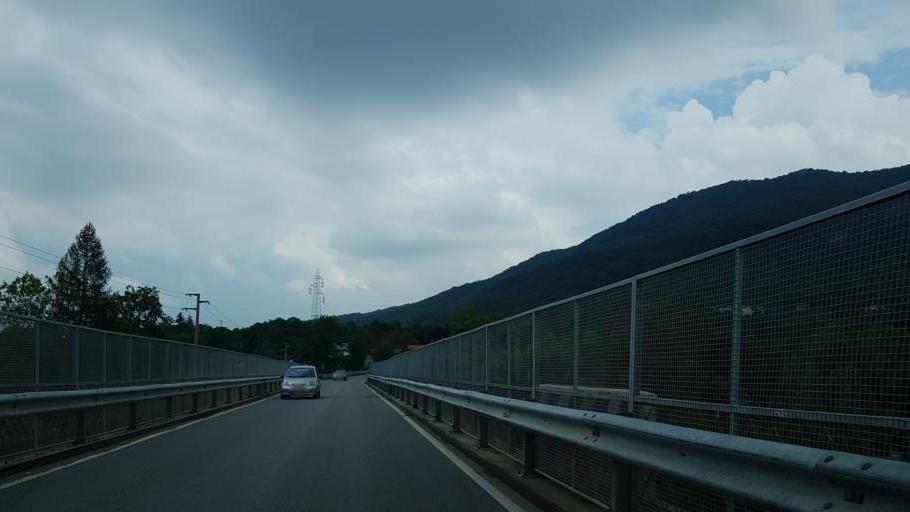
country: IT
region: Piedmont
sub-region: Provincia di Cuneo
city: Gaiola
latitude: 44.3367
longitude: 7.4167
